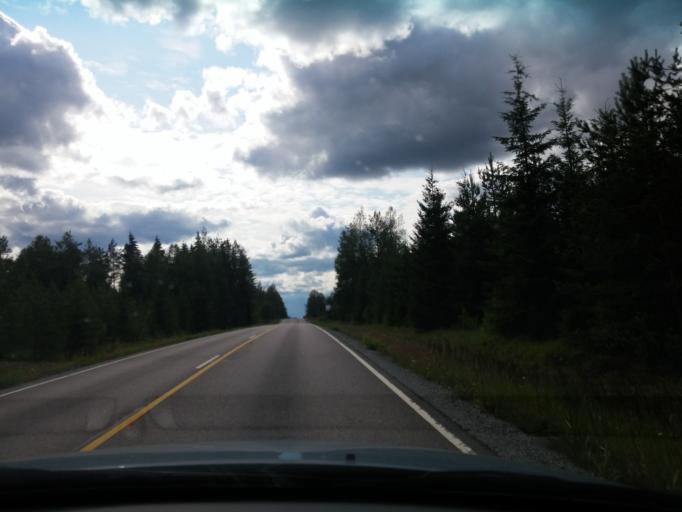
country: FI
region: Central Finland
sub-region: Saarijaervi-Viitasaari
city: Pylkoenmaeki
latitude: 62.6061
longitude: 24.6661
